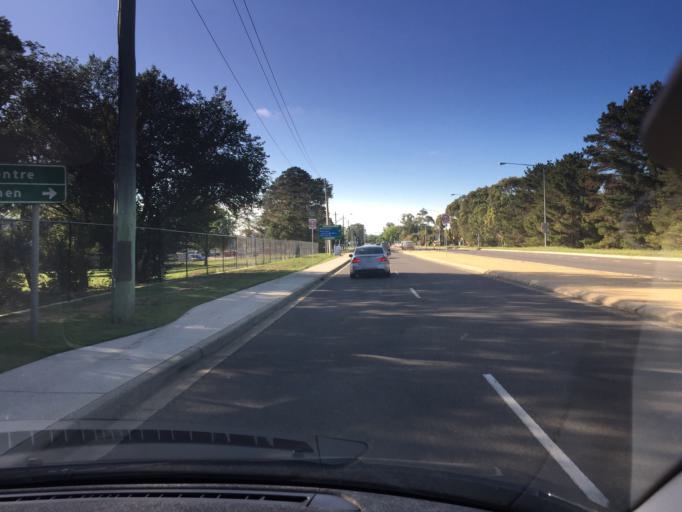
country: AU
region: Australian Capital Territory
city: Kaleen
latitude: -35.2408
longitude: 149.1261
